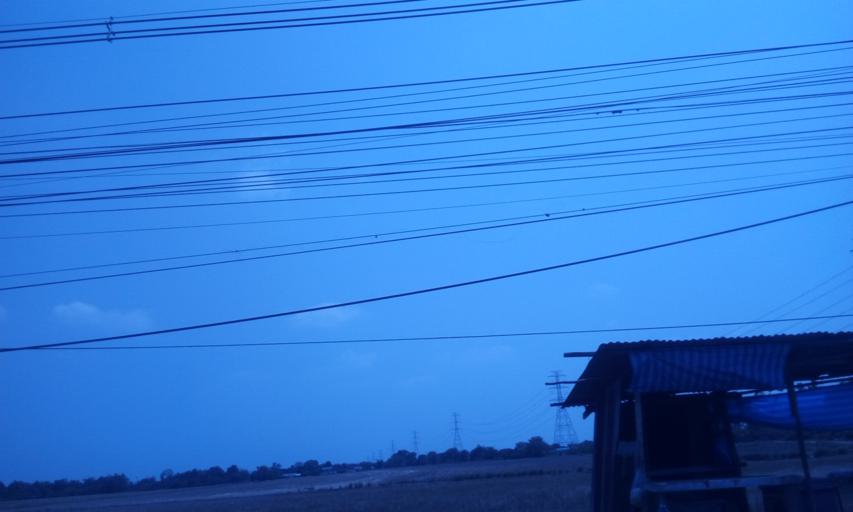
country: TH
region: Chachoengsao
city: Bang Nam Priao
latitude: 13.8276
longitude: 101.0554
